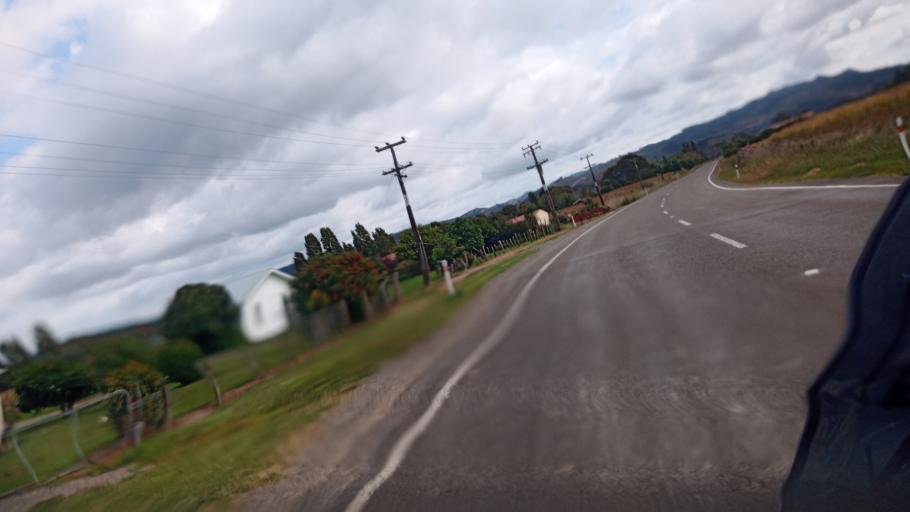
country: NZ
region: Gisborne
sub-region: Gisborne District
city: Gisborne
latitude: -38.3385
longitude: 178.2895
